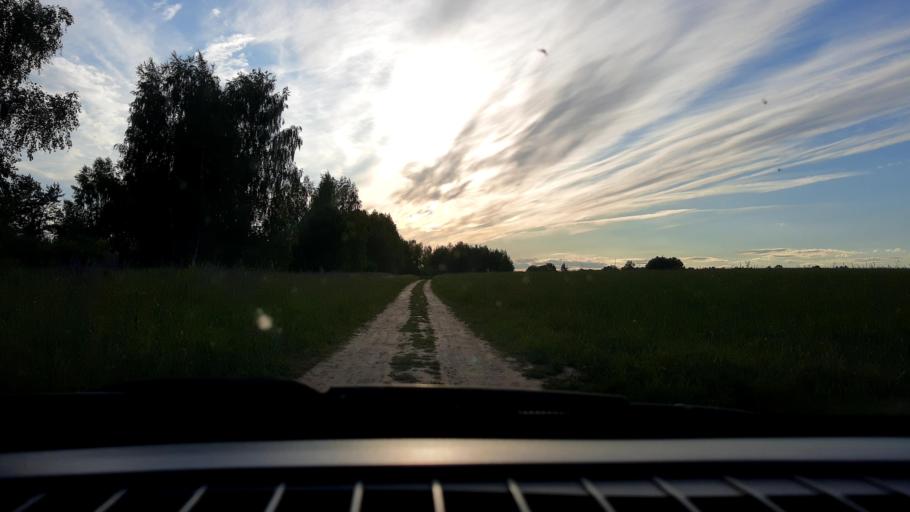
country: RU
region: Nizjnij Novgorod
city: Kstovo
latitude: 56.2640
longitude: 44.3138
